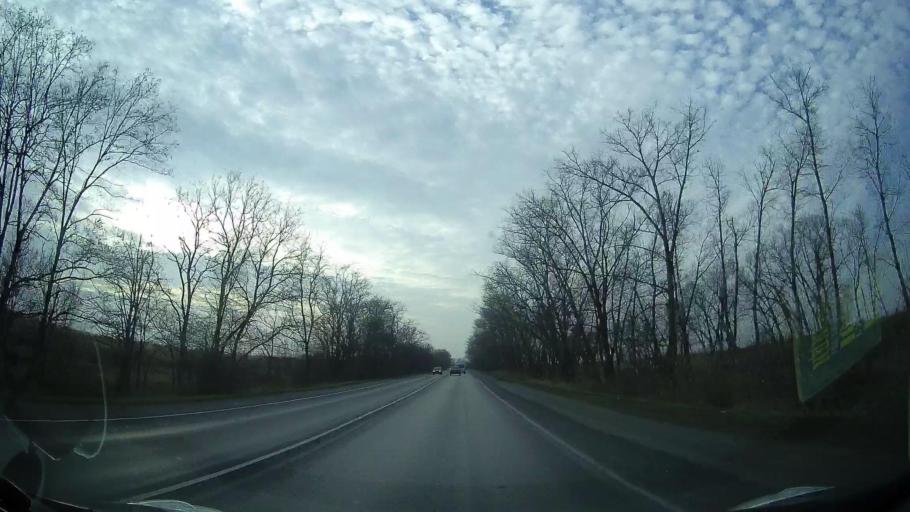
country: RU
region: Rostov
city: Starocherkasskaya
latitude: 47.1607
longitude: 40.2313
